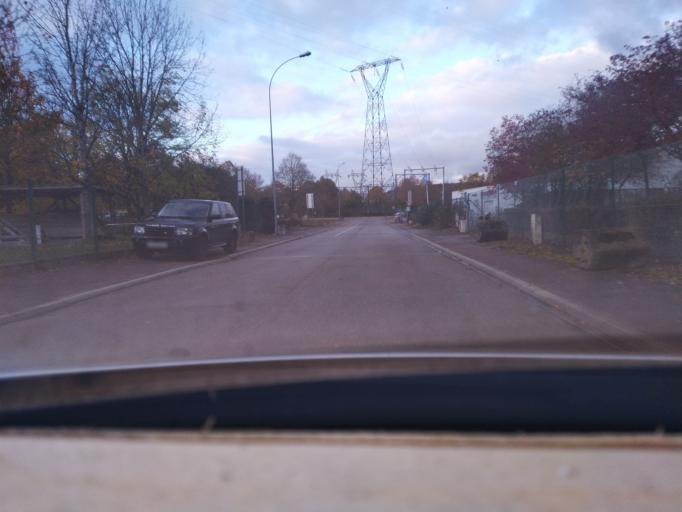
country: FR
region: Haute-Normandie
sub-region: Departement de la Seine-Maritime
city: Yainville
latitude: 49.4574
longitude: 0.8224
